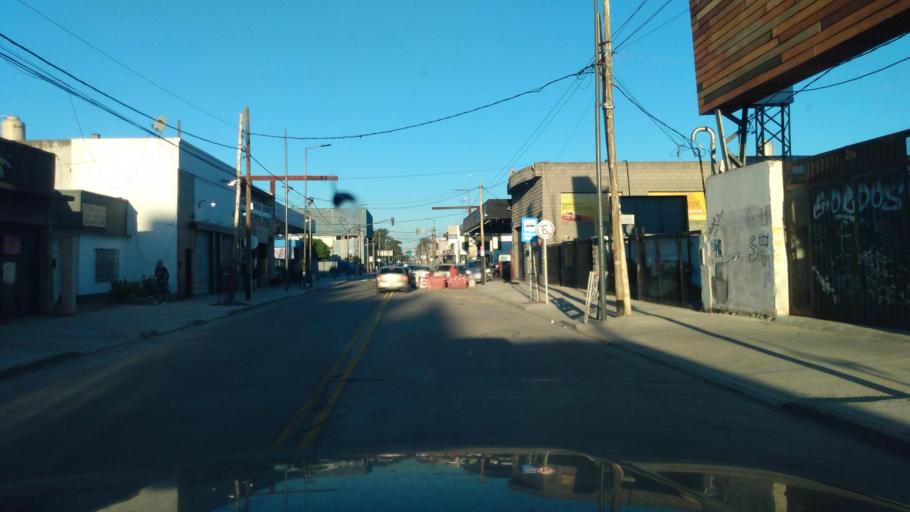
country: AR
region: Buenos Aires
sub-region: Partido de Merlo
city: Merlo
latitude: -34.6511
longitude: -58.7826
